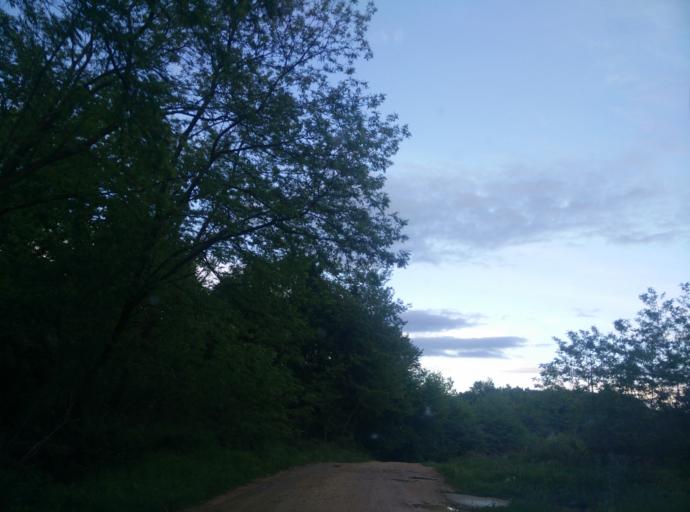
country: BA
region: Brcko
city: Brcko
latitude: 44.7795
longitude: 18.8302
